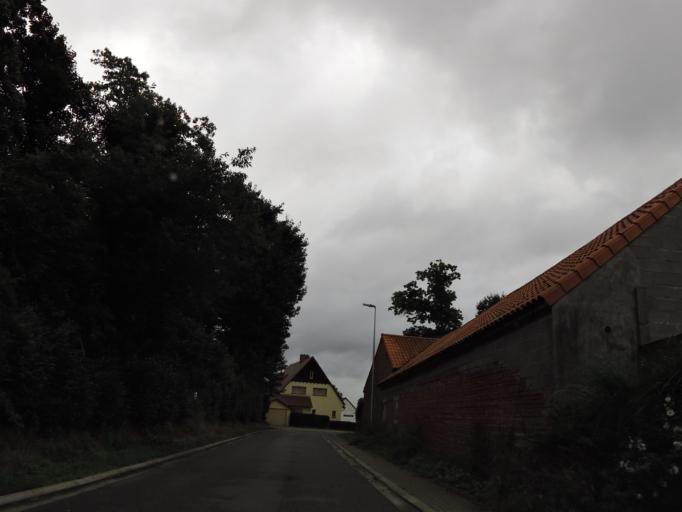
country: BE
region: Flanders
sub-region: Provincie Limburg
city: Bree
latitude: 51.1317
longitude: 5.5918
